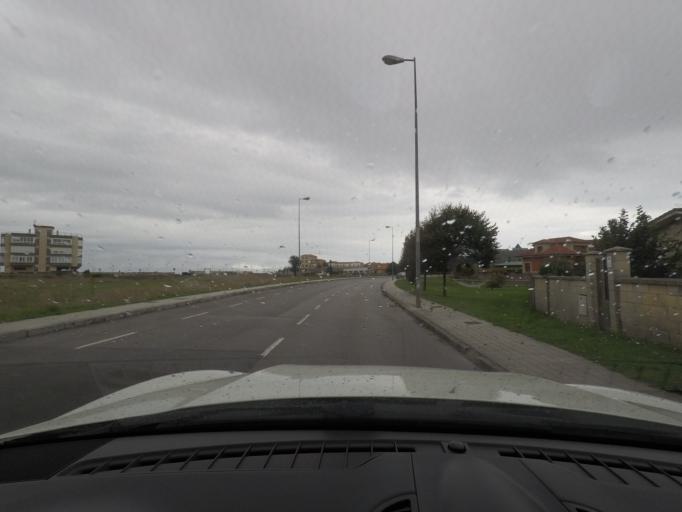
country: ES
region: Asturias
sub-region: Province of Asturias
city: Gijon
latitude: 43.5432
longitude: -5.6419
